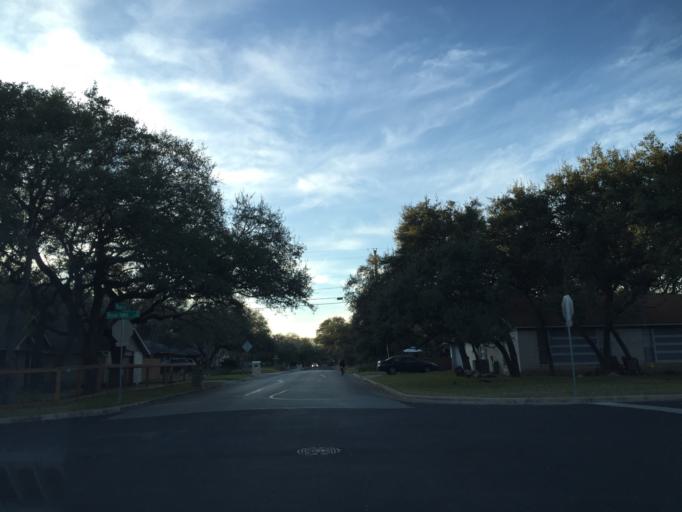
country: US
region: Texas
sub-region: Williamson County
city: Jollyville
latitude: 30.4253
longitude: -97.7633
